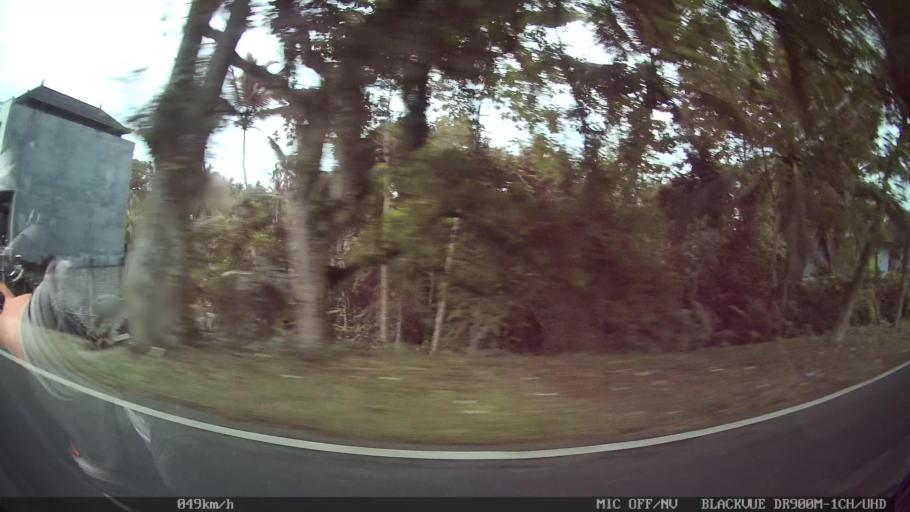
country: ID
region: Bali
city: Pohgending Kangin
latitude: -8.4279
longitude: 115.1442
